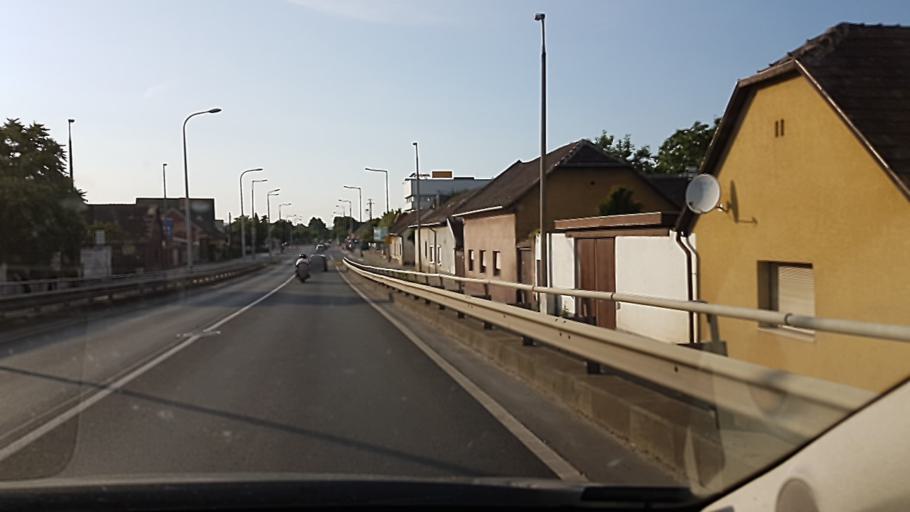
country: HU
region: Budapest
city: Budapest XXIII. keruelet
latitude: 47.3879
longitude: 19.1216
